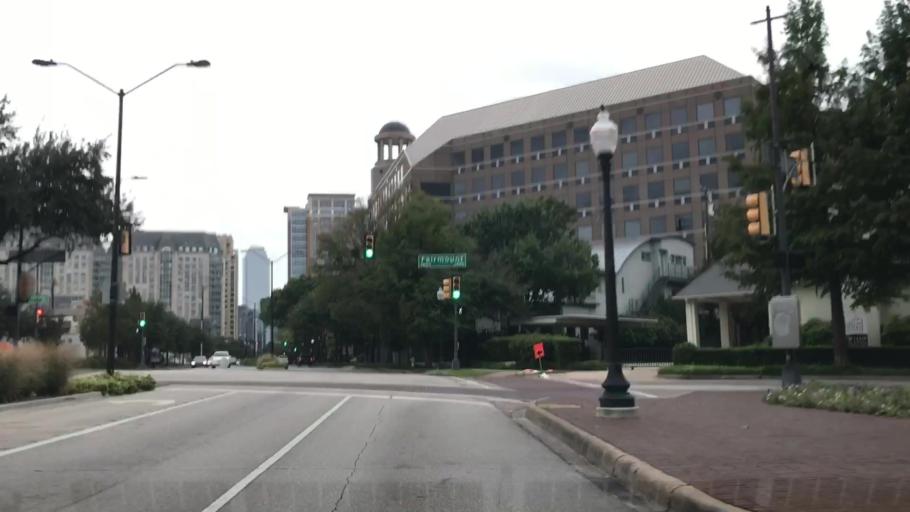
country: US
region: Texas
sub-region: Dallas County
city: Dallas
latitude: 32.7983
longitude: -96.8056
